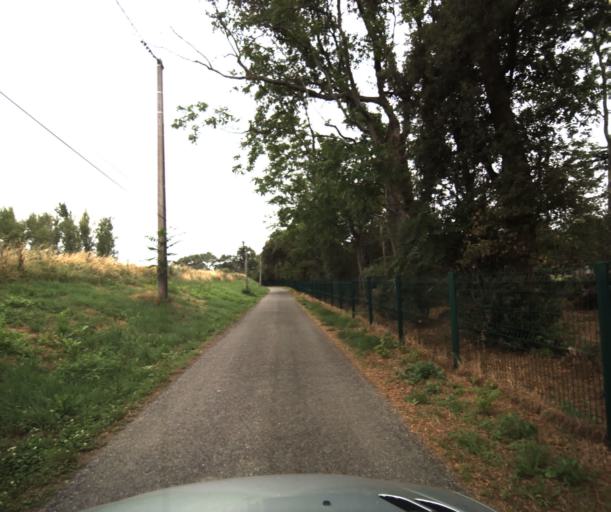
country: FR
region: Midi-Pyrenees
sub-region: Departement de la Haute-Garonne
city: Pinsaguel
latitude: 43.5046
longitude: 1.3861
